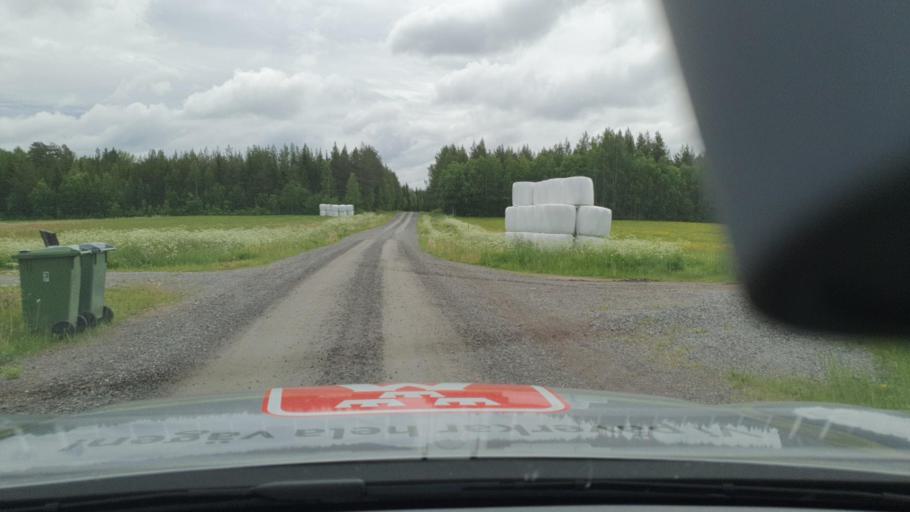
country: SE
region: Norrbotten
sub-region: Lulea Kommun
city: Ranea
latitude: 65.9710
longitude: 22.0577
